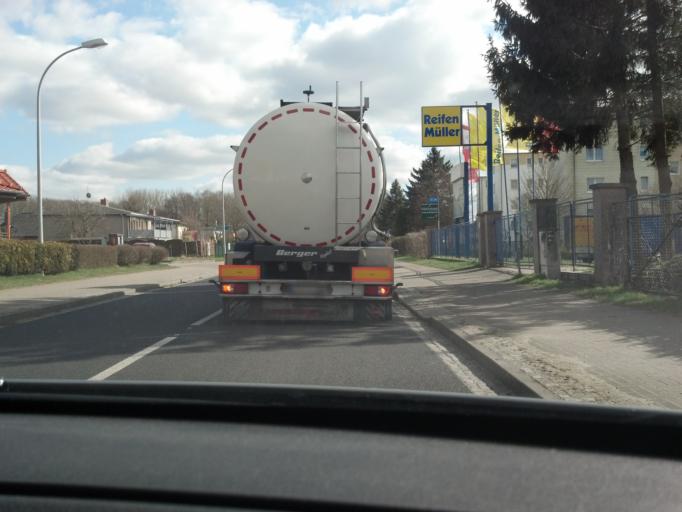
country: DE
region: Brandenburg
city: Gerdshagen
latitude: 53.3200
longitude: 12.2401
